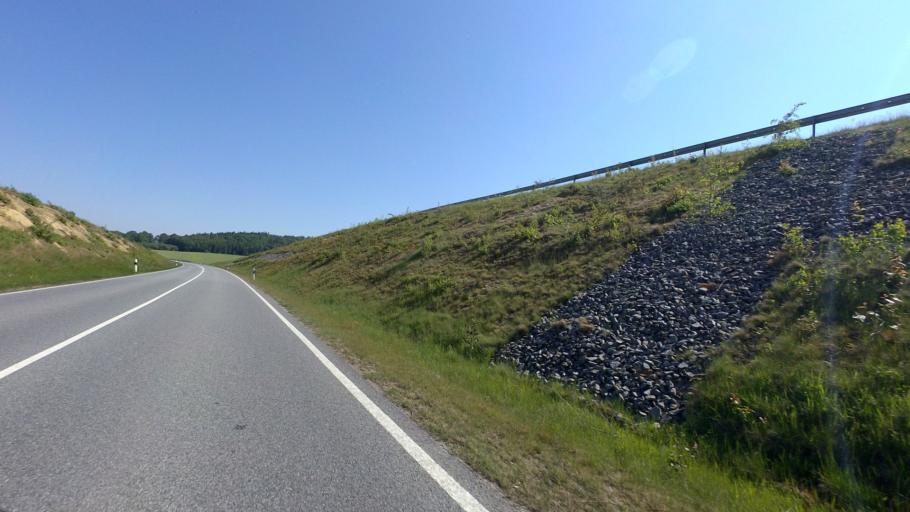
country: DE
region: Saxony
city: Elstra
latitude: 51.1960
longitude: 14.1484
